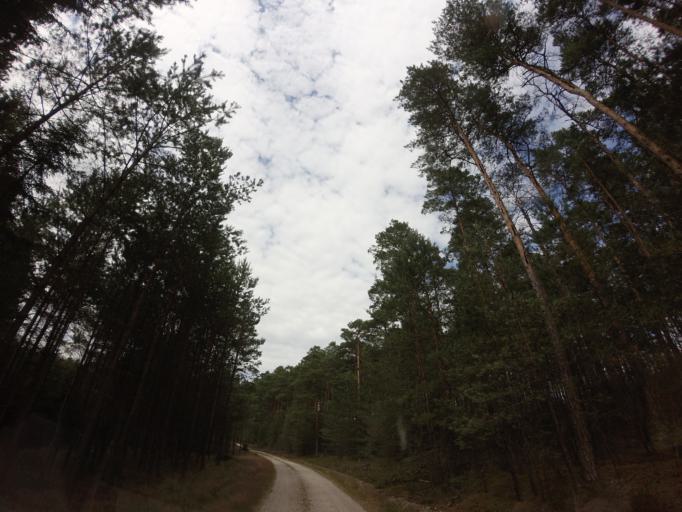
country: PL
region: West Pomeranian Voivodeship
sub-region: Powiat choszczenski
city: Drawno
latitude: 53.1563
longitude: 15.7581
